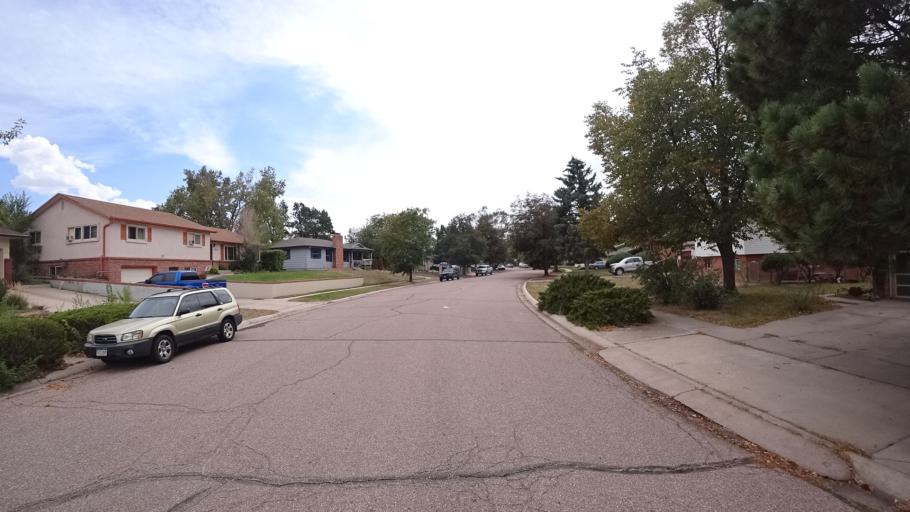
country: US
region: Colorado
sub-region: El Paso County
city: Colorado Springs
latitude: 38.8664
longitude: -104.7823
